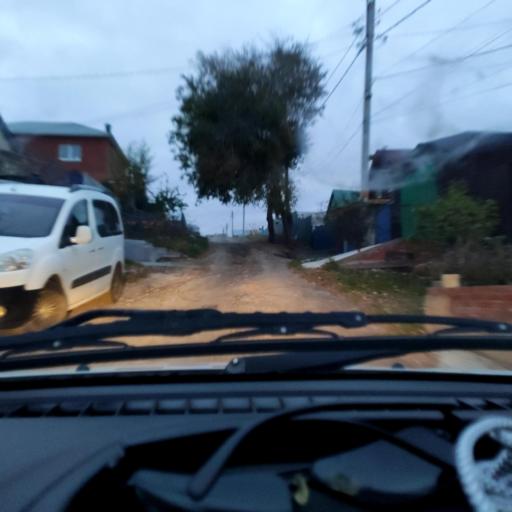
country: RU
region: Samara
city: Zhigulevsk
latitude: 53.4844
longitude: 49.5230
